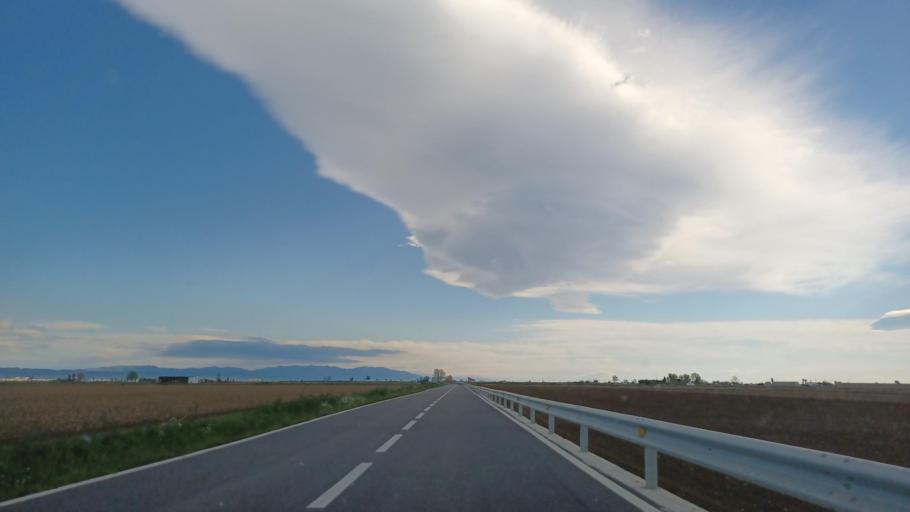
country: ES
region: Catalonia
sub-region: Provincia de Tarragona
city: Deltebre
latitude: 40.7341
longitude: 0.7118
